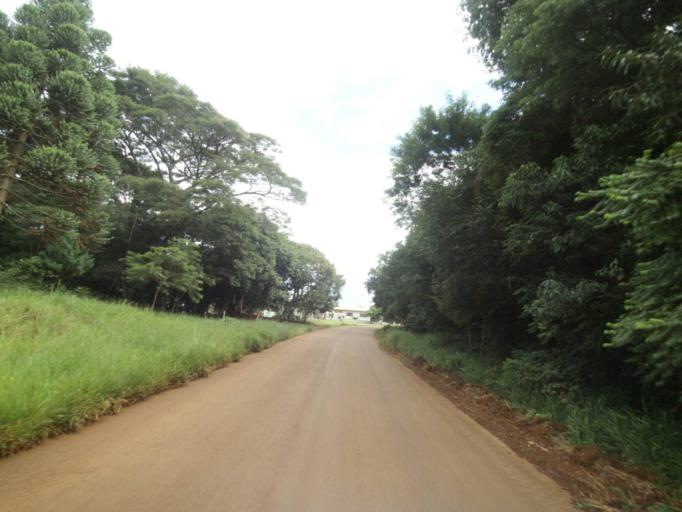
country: BR
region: Parana
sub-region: Pitanga
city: Pitanga
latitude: -24.9060
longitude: -52.0341
